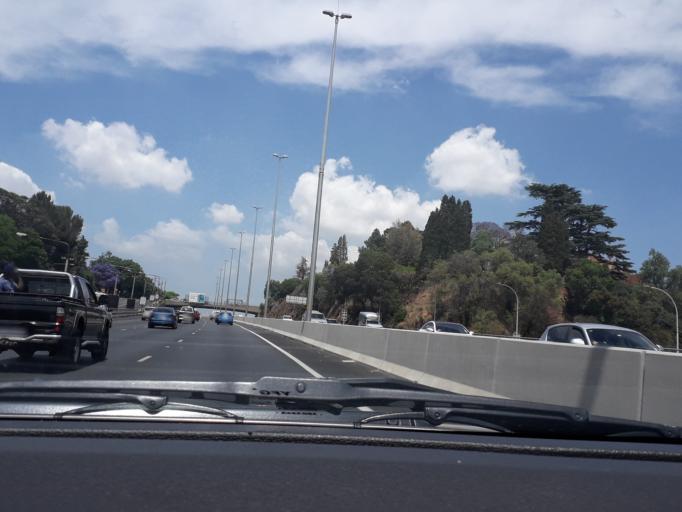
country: ZA
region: Gauteng
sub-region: City of Johannesburg Metropolitan Municipality
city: Johannesburg
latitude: -26.1763
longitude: 28.0382
